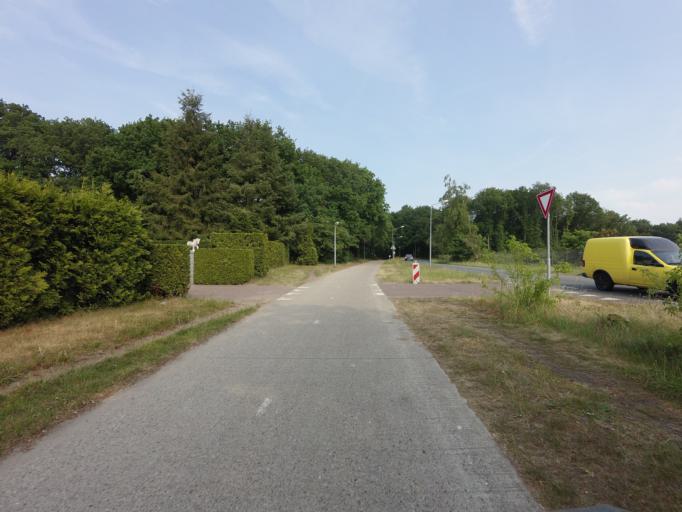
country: NL
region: North Holland
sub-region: Gemeente Wijdemeren
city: Nieuw-Loosdrecht
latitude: 52.1983
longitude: 5.1482
